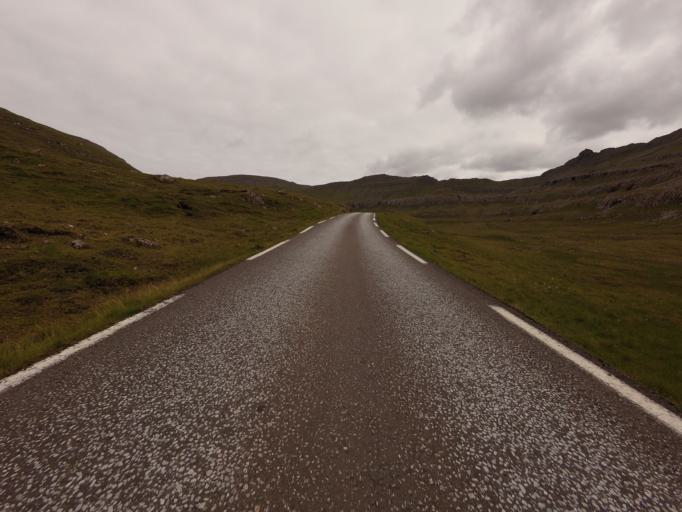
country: FO
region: Suduroy
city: Tvoroyri
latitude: 61.5168
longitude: -6.8721
